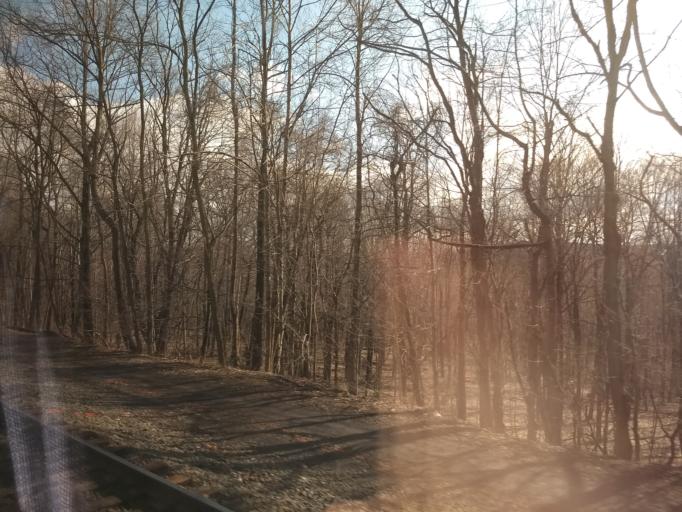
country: US
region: Pennsylvania
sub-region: Blair County
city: Duncansville
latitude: 40.4818
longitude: -78.4769
